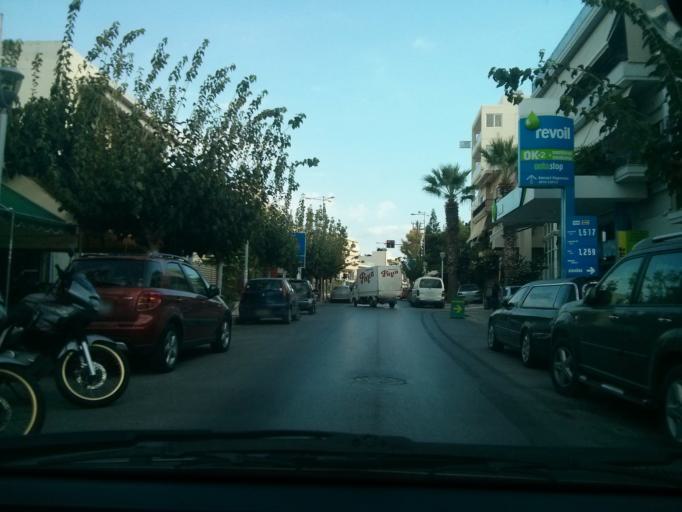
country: GR
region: Crete
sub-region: Nomos Irakleiou
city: Irakleion
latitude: 35.3291
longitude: 25.1372
